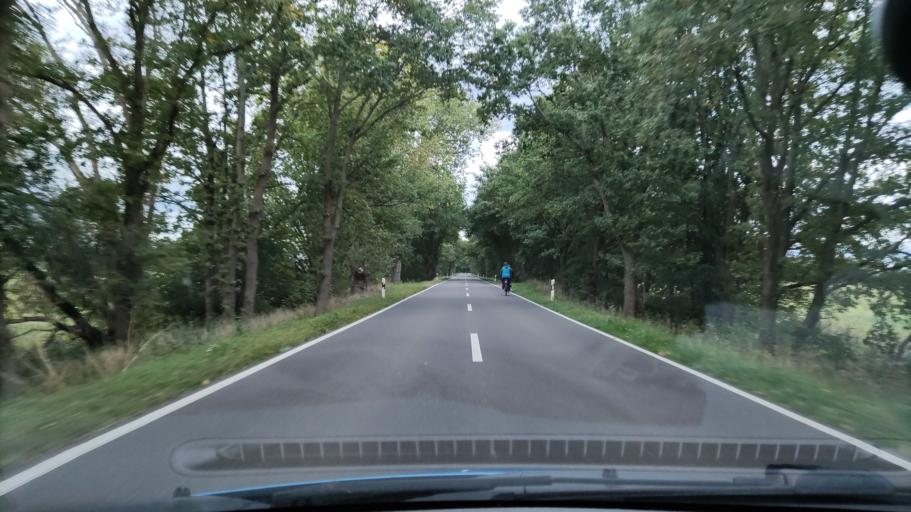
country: DE
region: Lower Saxony
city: Neu Darchau
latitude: 53.3399
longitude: 10.9511
